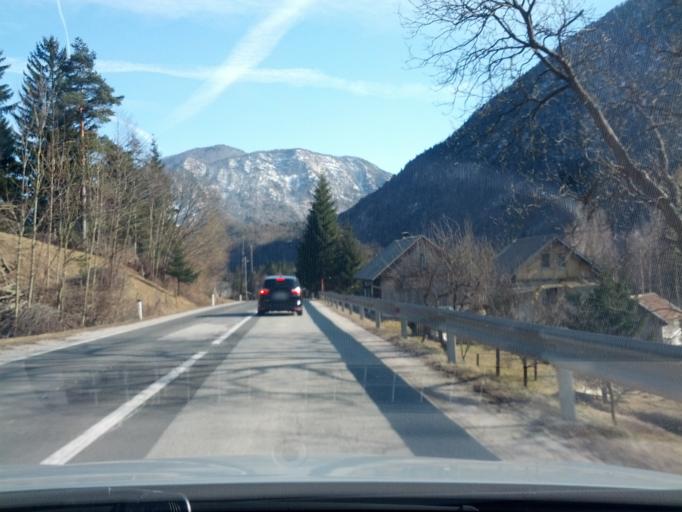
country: SI
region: Kranjska Gora
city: Mojstrana
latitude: 46.4736
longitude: 13.9134
